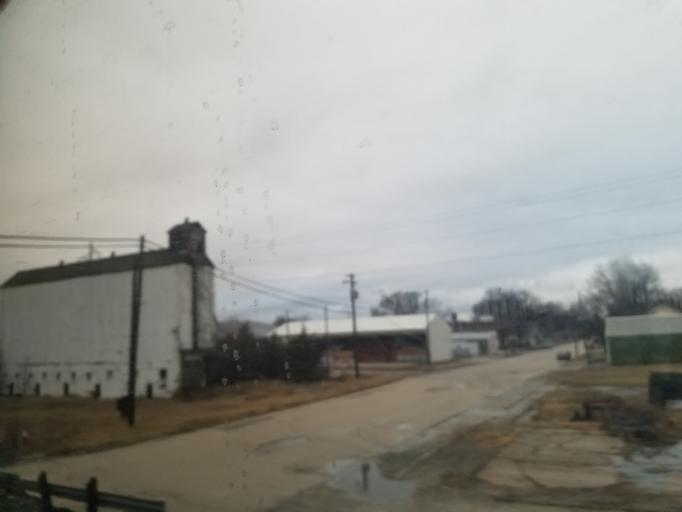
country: US
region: Illinois
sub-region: Warren County
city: Monmouth
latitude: 40.9065
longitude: -90.6433
